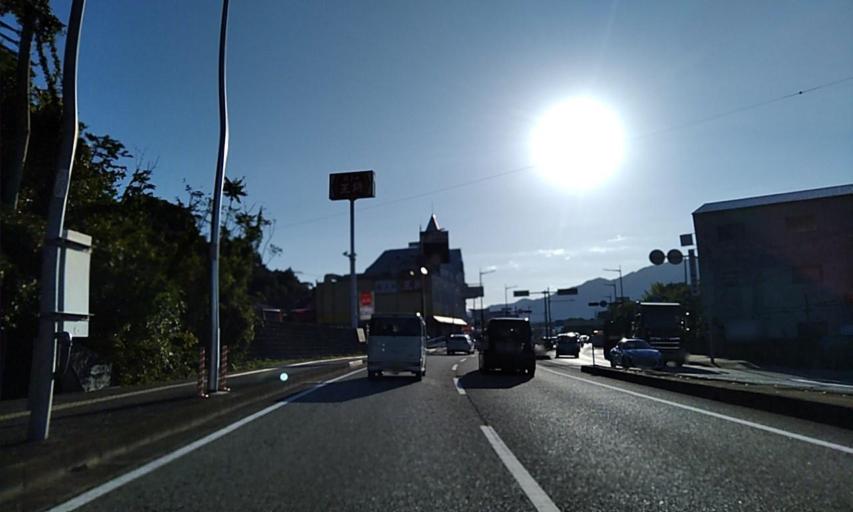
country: JP
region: Wakayama
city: Kainan
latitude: 34.1604
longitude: 135.1921
